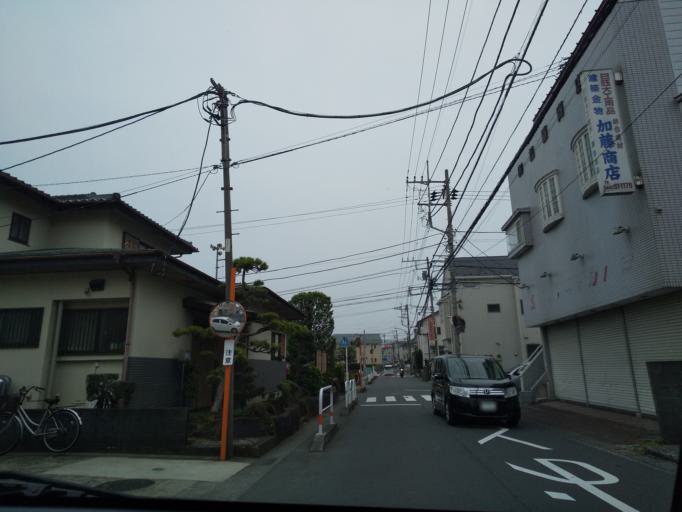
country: JP
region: Kanagawa
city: Zama
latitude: 35.5007
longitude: 139.4049
